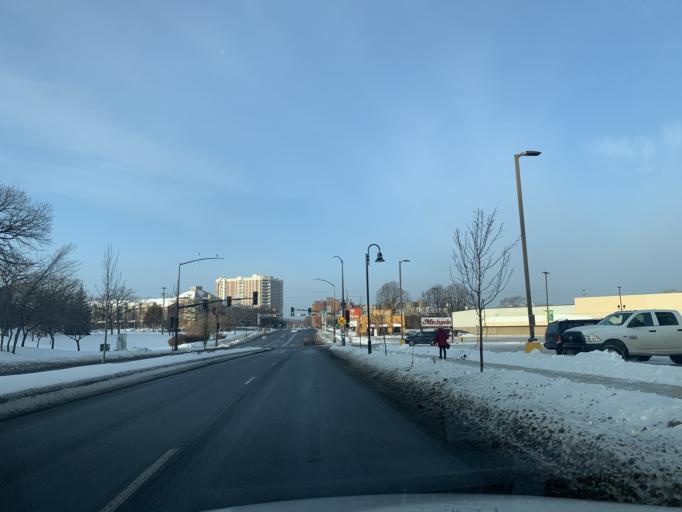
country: US
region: Minnesota
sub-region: Hennepin County
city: Richfield
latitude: 44.8835
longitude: -93.2808
